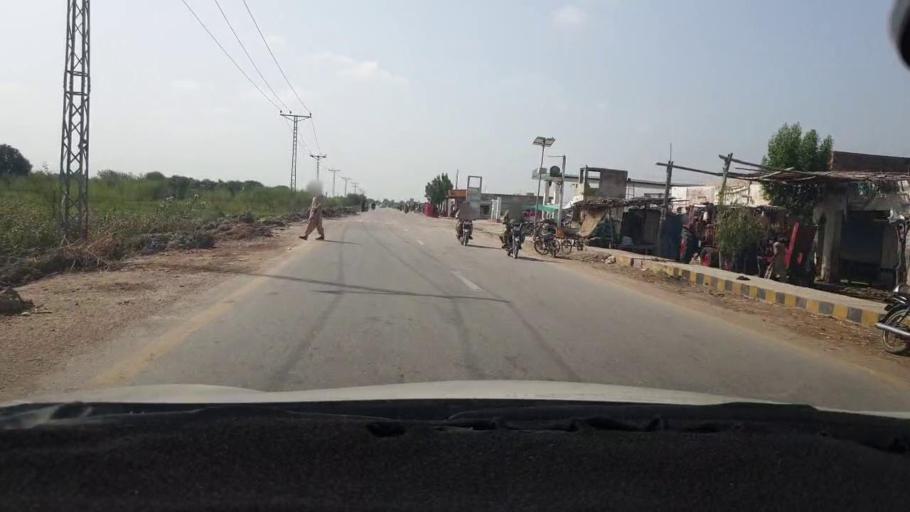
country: PK
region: Sindh
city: Mirpur Khas
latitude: 25.7719
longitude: 69.0713
